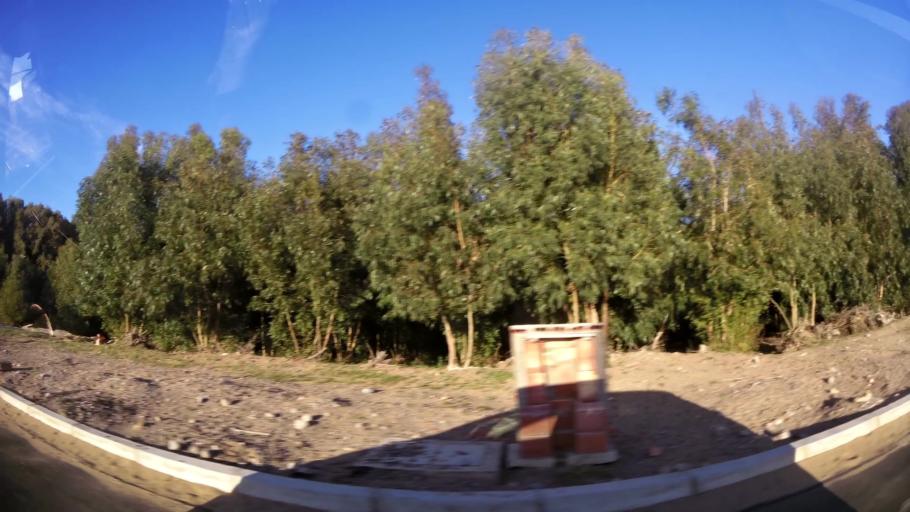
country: MA
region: Oriental
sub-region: Berkane-Taourirt
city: Madagh
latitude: 35.0781
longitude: -2.2412
